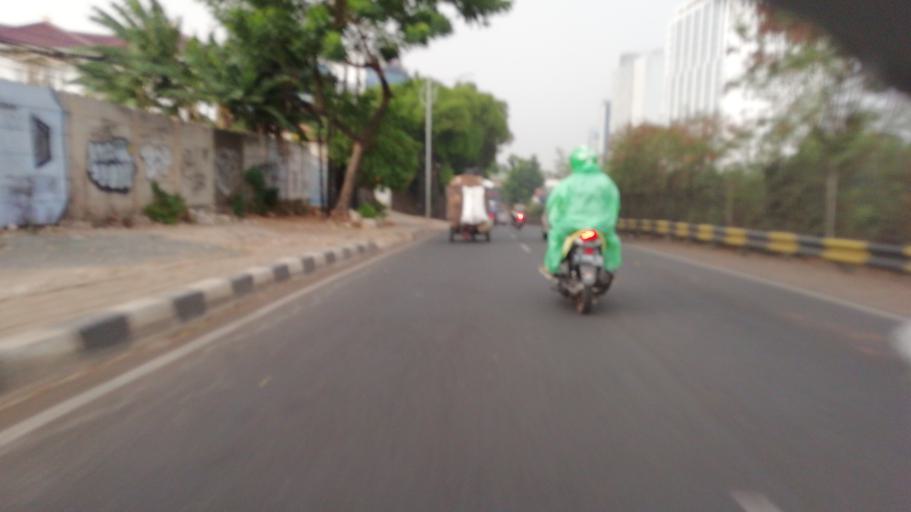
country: ID
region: Jakarta Raya
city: Jakarta
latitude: -6.2962
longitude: 106.8279
